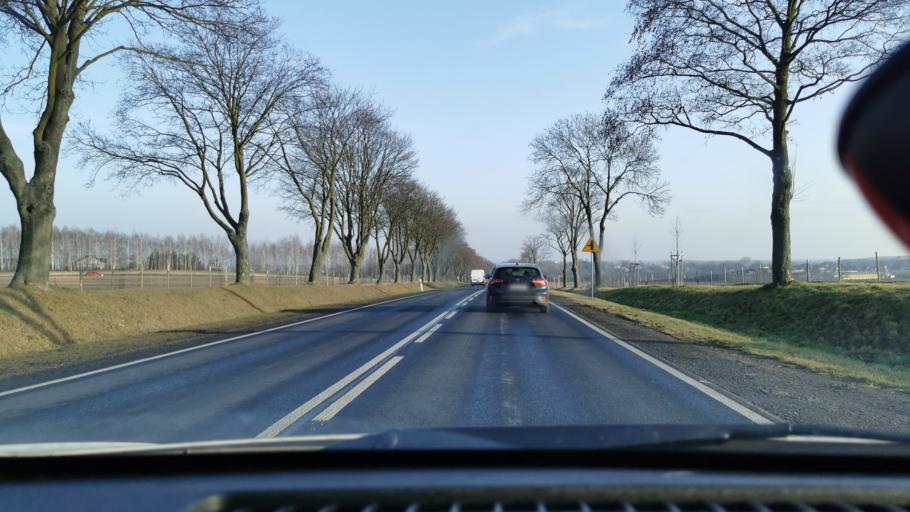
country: PL
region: Lodz Voivodeship
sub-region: Powiat sieradzki
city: Wroblew
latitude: 51.6167
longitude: 18.5986
